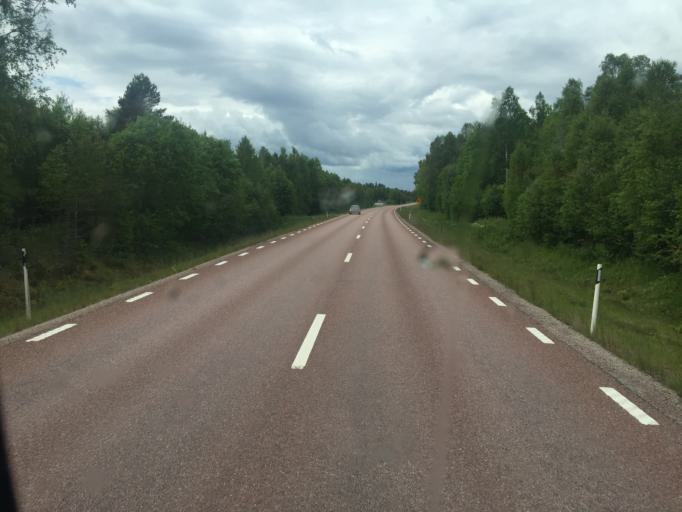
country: SE
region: Dalarna
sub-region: Vansbro Kommun
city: Vansbro
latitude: 60.4841
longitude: 14.0359
